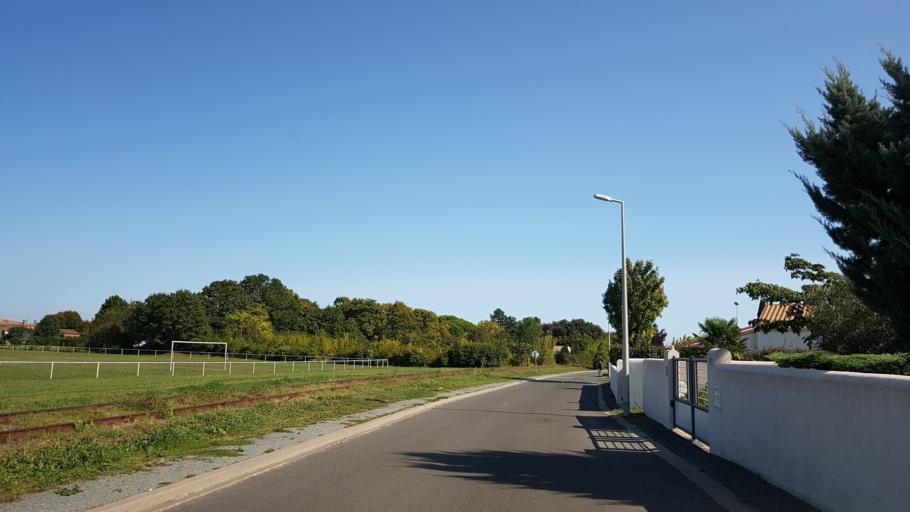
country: FR
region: Poitou-Charentes
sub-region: Departement de la Charente-Maritime
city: Breuillet
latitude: 45.7092
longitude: -1.0339
